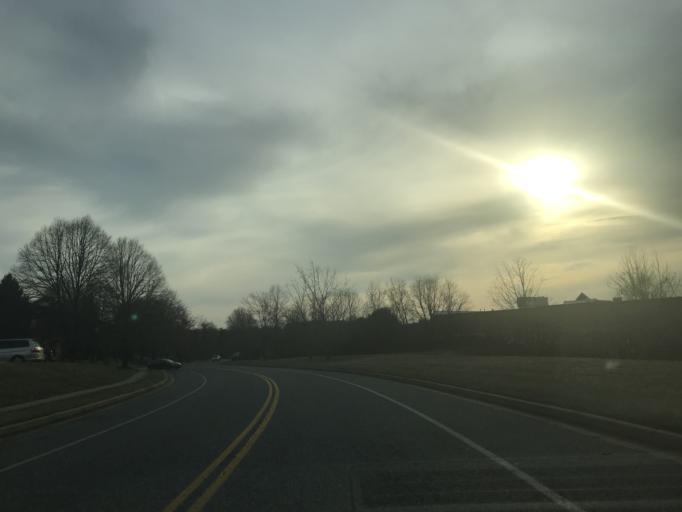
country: US
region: Maryland
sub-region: Harford County
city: South Bel Air
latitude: 39.5418
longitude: -76.3220
